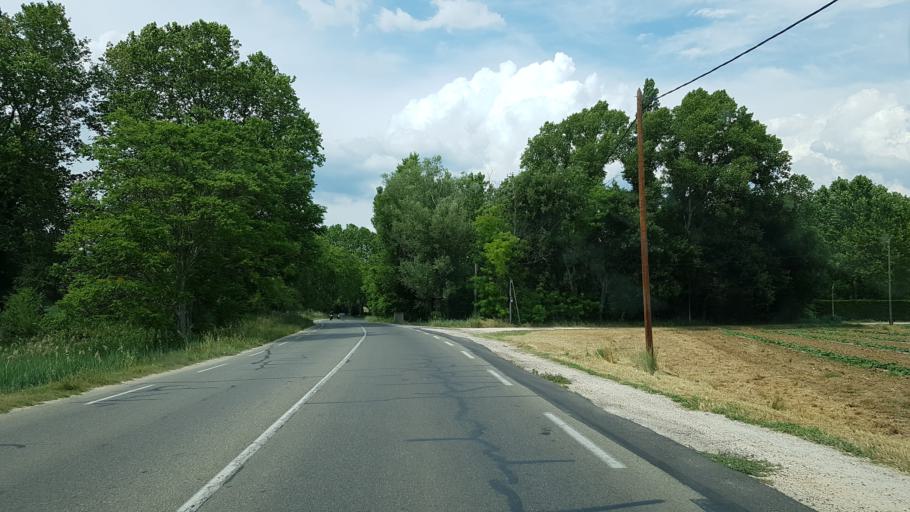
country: FR
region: Provence-Alpes-Cote d'Azur
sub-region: Departement du Vaucluse
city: Apt
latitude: 43.8990
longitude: 5.3831
